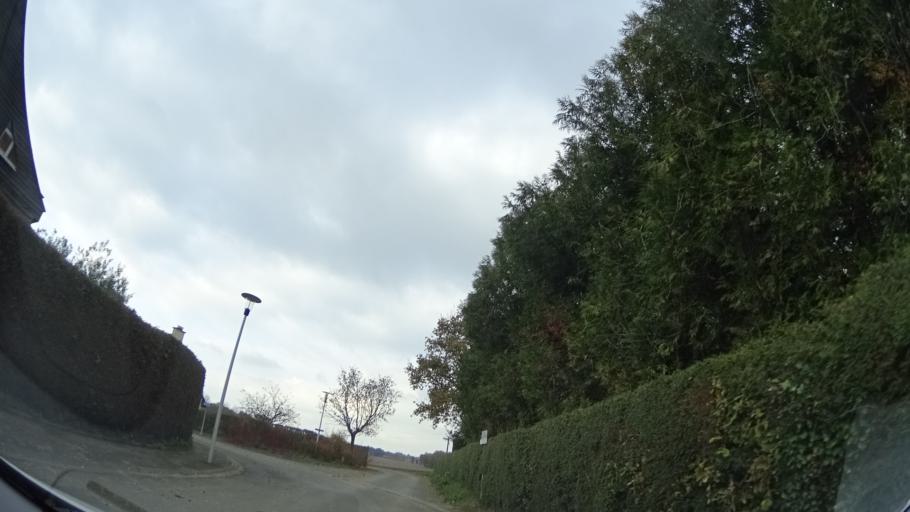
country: FR
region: Brittany
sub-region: Departement d'Ille-et-Vilaine
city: Montgermont
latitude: 48.1608
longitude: -1.7144
